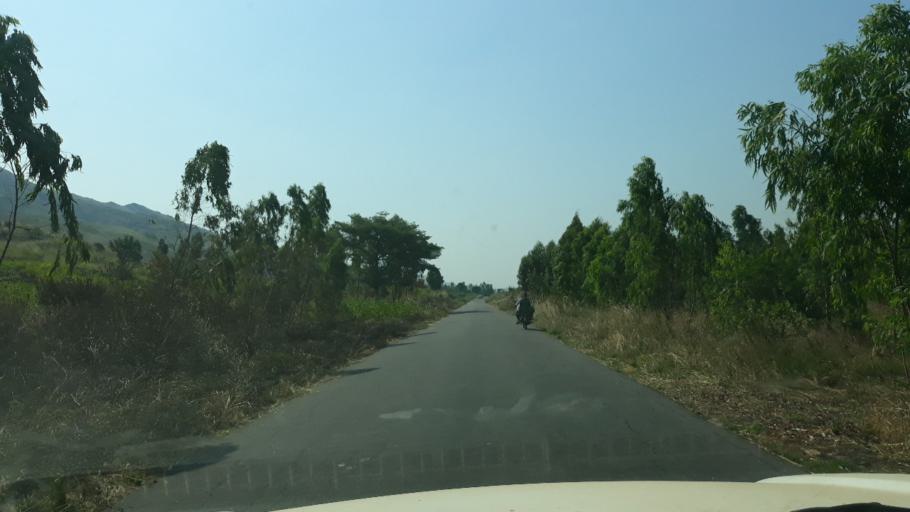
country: CD
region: South Kivu
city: Uvira
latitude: -3.2624
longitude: 29.1614
